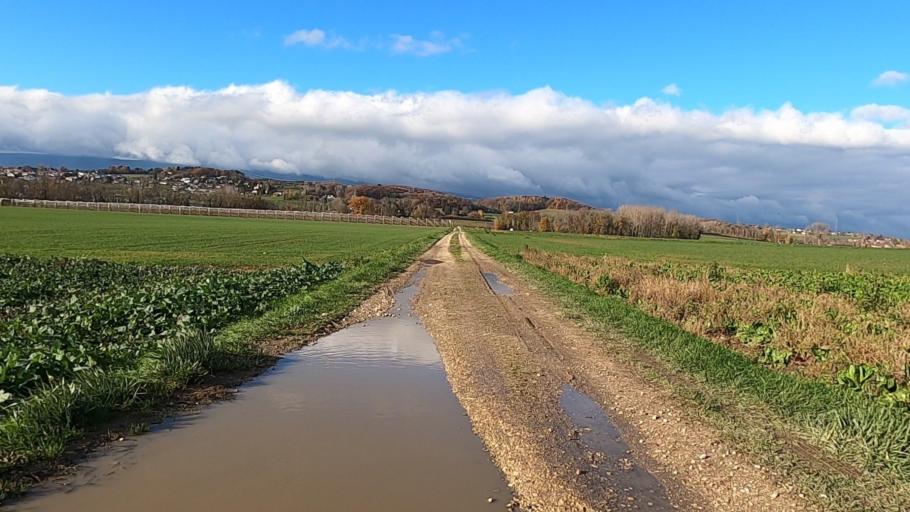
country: CH
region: Vaud
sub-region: Morges District
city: Apples
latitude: 46.5165
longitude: 6.4420
